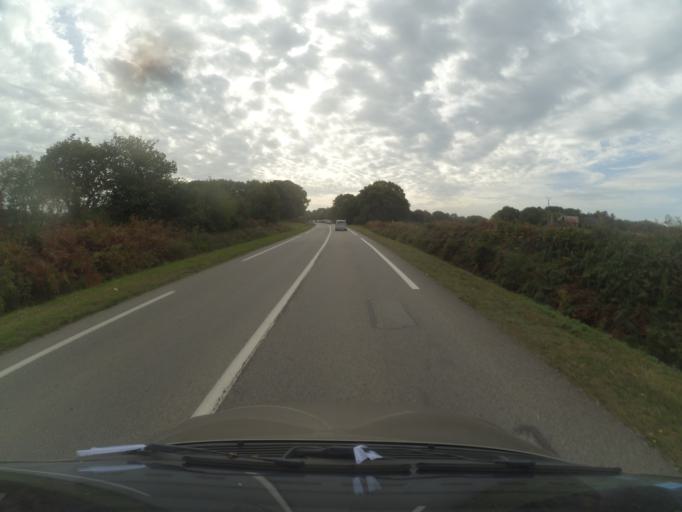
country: FR
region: Brittany
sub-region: Departement du Morbihan
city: Merlevenez
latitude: 47.7213
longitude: -3.2301
